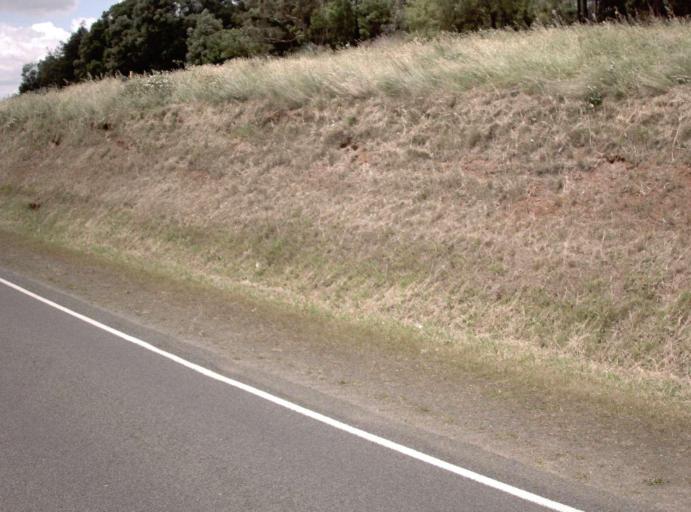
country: AU
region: Victoria
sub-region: Baw Baw
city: Warragul
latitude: -38.1680
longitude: 145.9617
